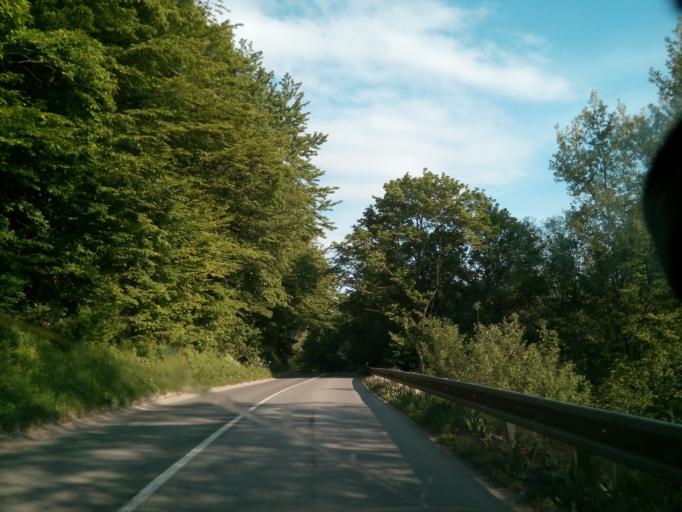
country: SK
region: Kosicky
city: Kosice
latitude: 48.7618
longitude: 21.2460
